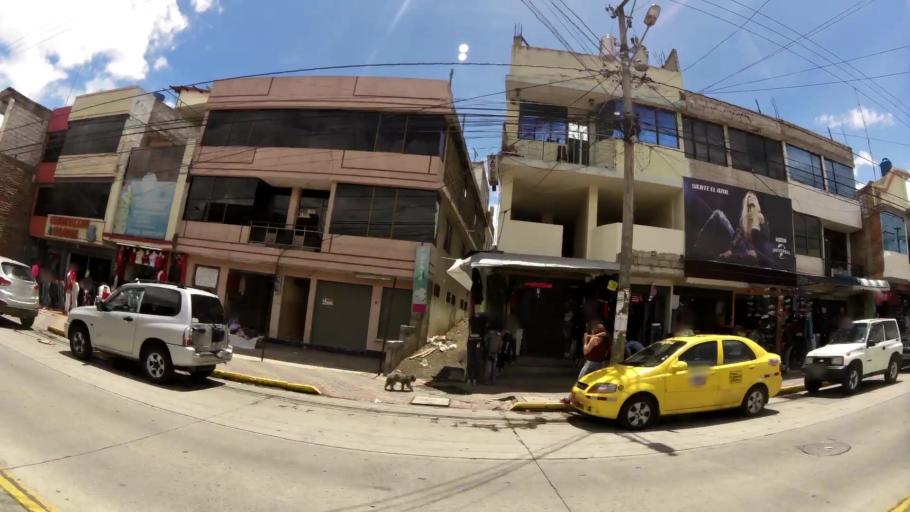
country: EC
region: Tungurahua
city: Pelileo
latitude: -1.3326
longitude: -78.5527
